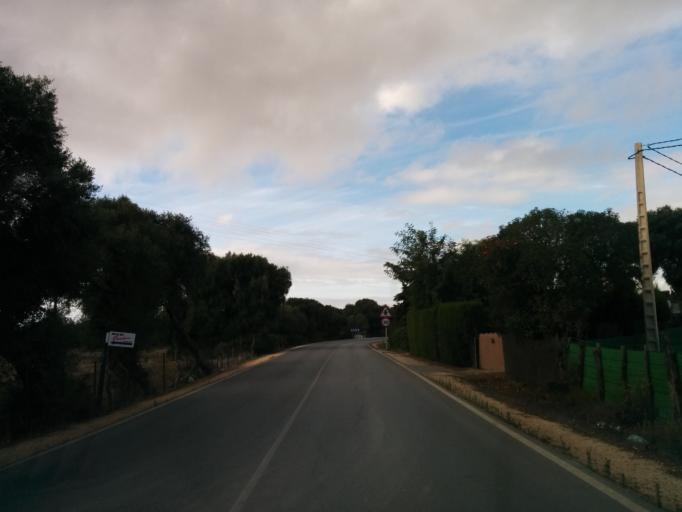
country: ES
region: Andalusia
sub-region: Provincia de Cadiz
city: Vejer de la Frontera
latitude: 36.2067
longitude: -6.0350
